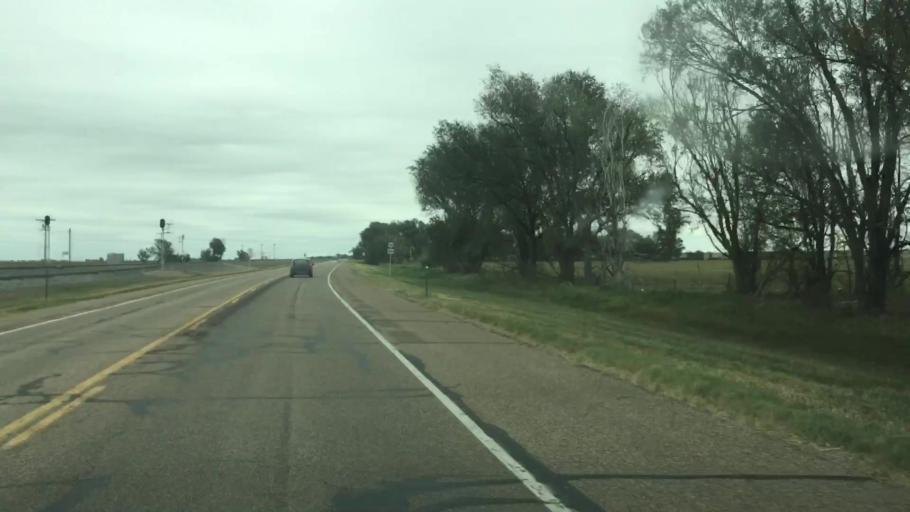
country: US
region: Colorado
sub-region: Prowers County
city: Lamar
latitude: 38.0614
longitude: -102.3011
